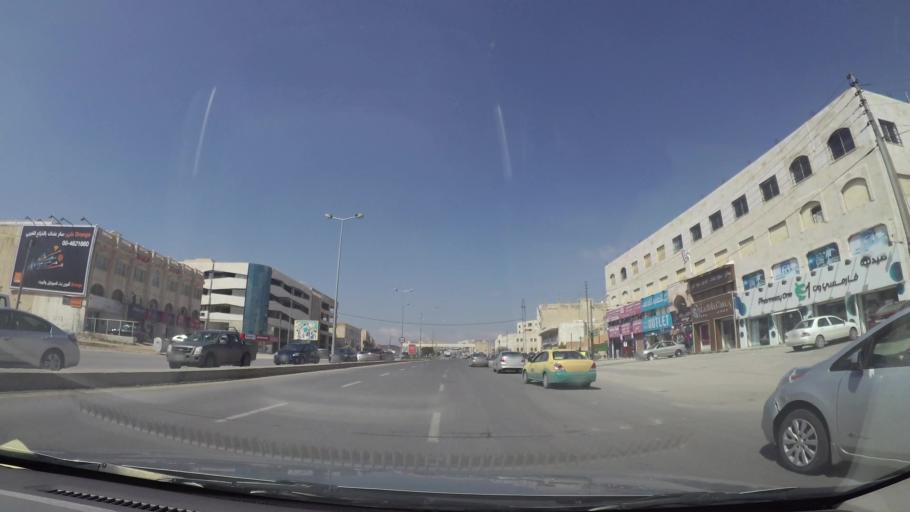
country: JO
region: Amman
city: Al Bunayyat ash Shamaliyah
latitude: 31.9000
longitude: 35.8954
